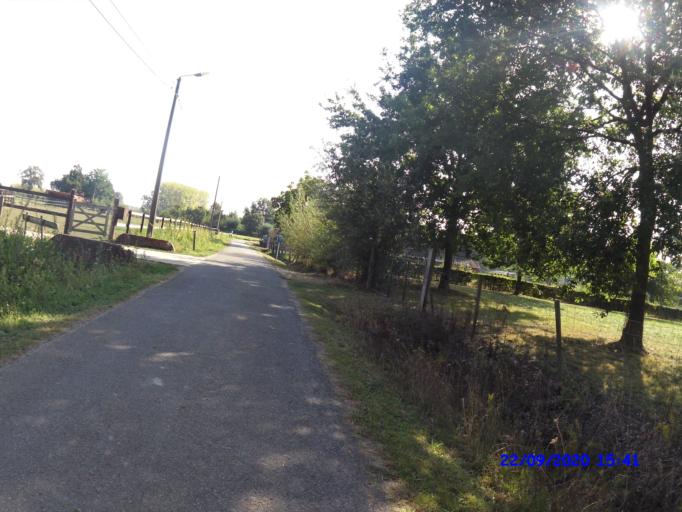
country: BE
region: Flanders
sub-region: Provincie Limburg
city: Alken
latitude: 50.8854
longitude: 5.3226
